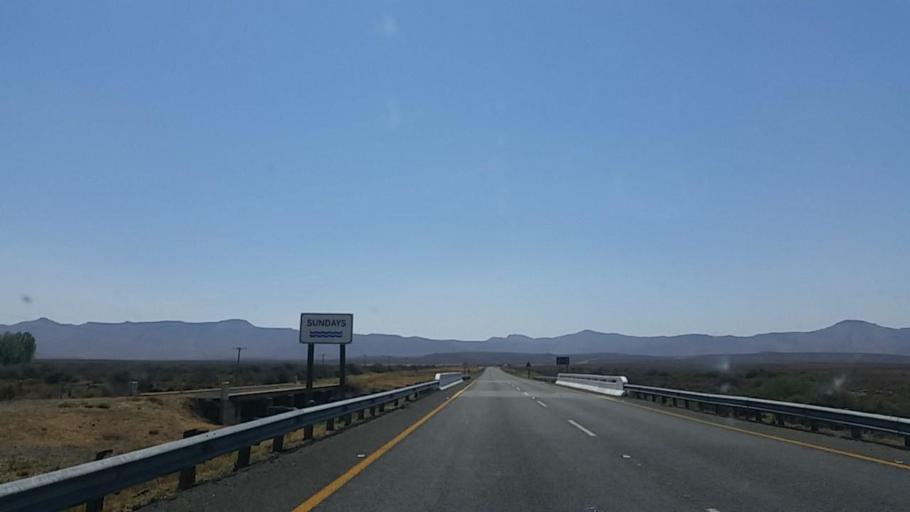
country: ZA
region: Eastern Cape
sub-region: Cacadu District Municipality
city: Graaff-Reinet
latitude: -31.9003
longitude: 24.7802
